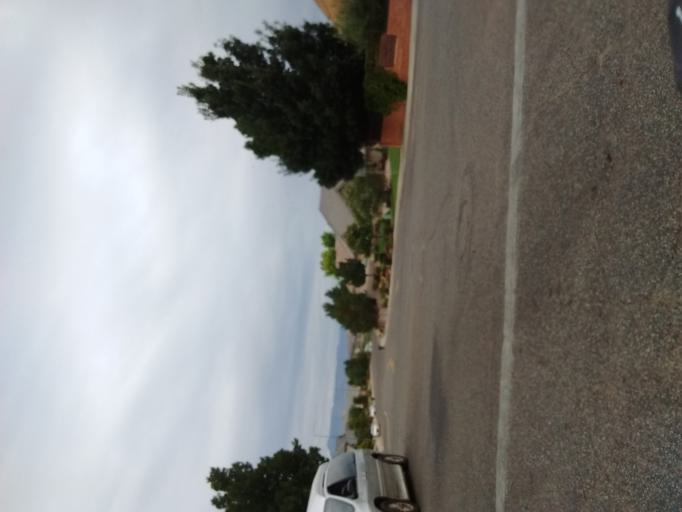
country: US
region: Utah
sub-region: Washington County
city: Saint George
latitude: 37.0925
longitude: -113.5643
